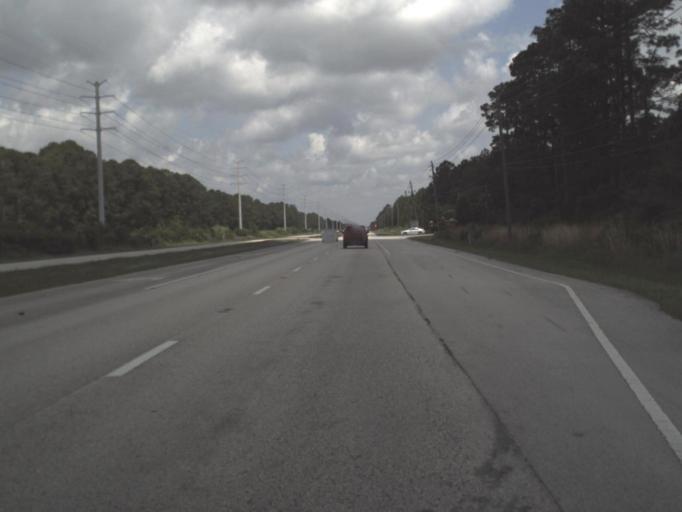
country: US
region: Florida
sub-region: Saint Johns County
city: Villano Beach
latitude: 30.0206
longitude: -81.3992
